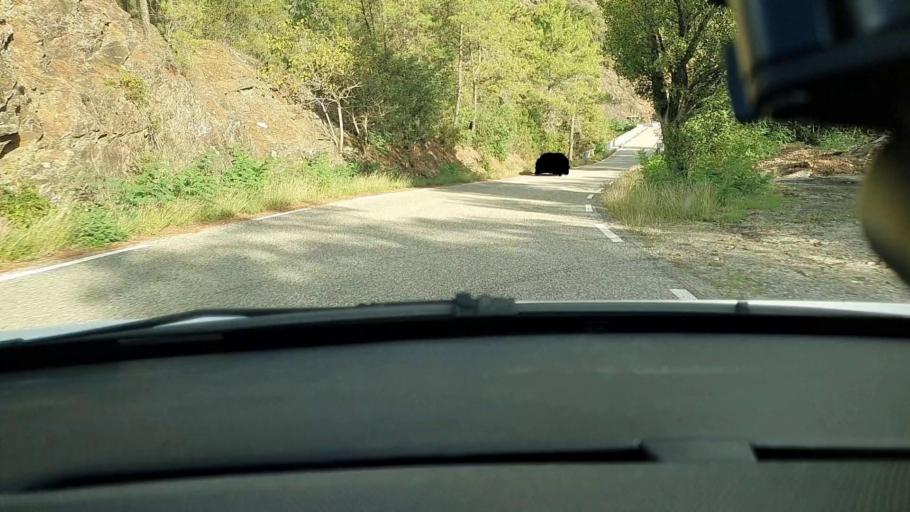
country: FR
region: Languedoc-Roussillon
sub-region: Departement du Gard
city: Besseges
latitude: 44.3180
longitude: 4.0382
